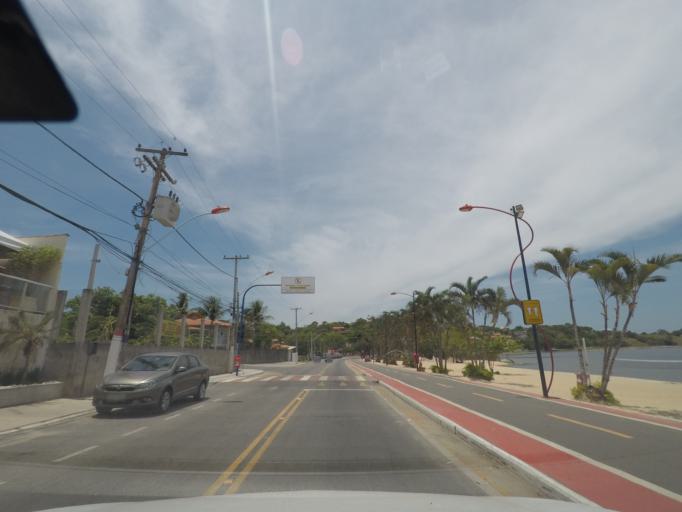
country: BR
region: Rio de Janeiro
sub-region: Marica
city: Marica
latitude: -22.9266
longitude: -42.8272
